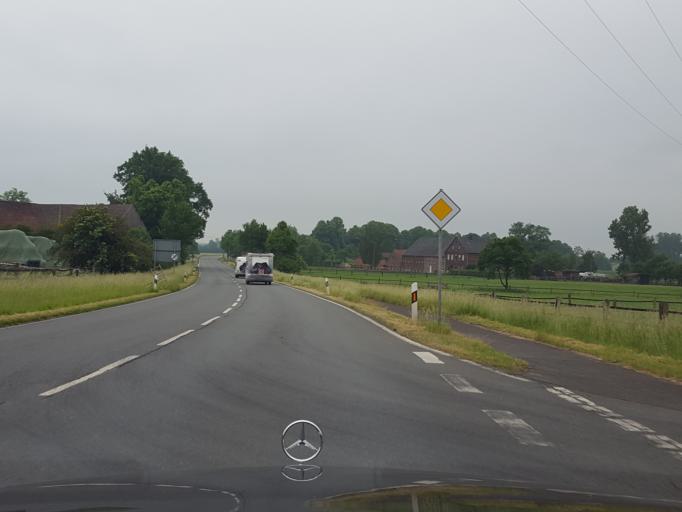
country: DE
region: North Rhine-Westphalia
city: Olfen
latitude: 51.7197
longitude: 7.4039
